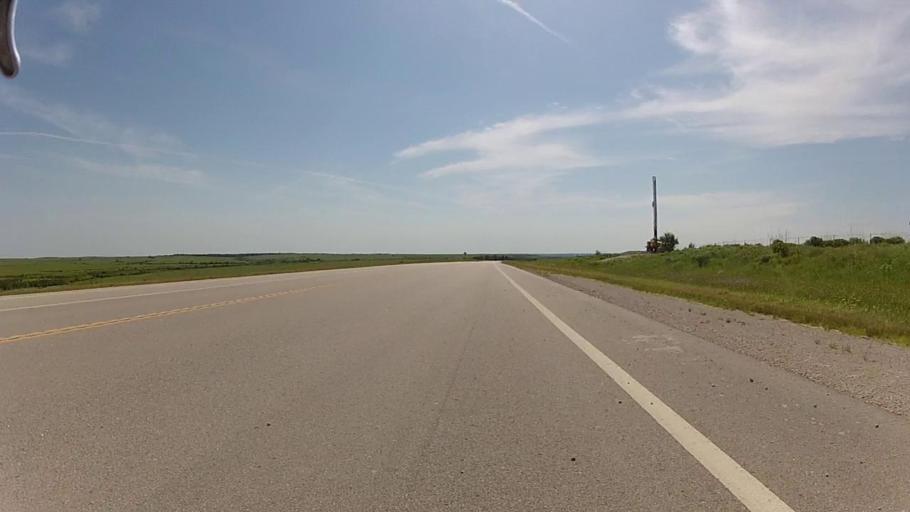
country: US
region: Kansas
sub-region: Cowley County
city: Winfield
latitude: 37.1111
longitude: -96.6058
